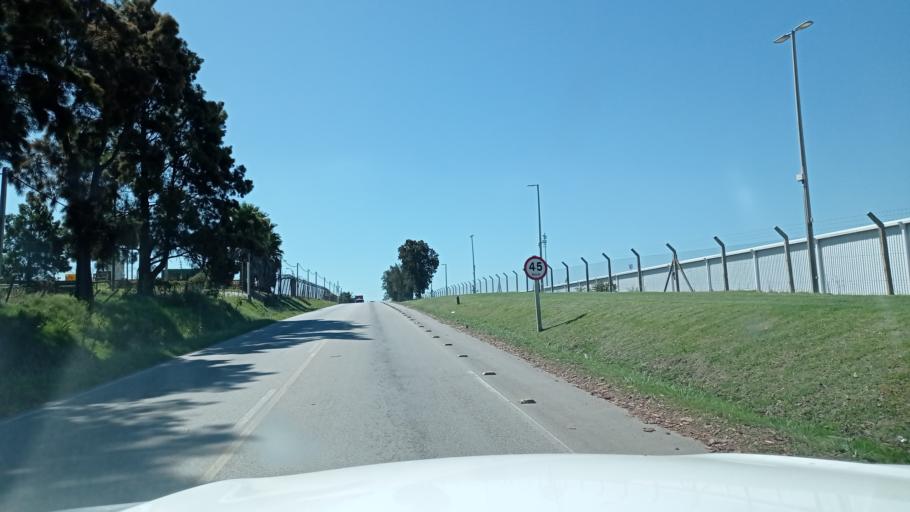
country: UY
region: Montevideo
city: Pajas Blancas
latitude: -34.8565
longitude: -56.2894
